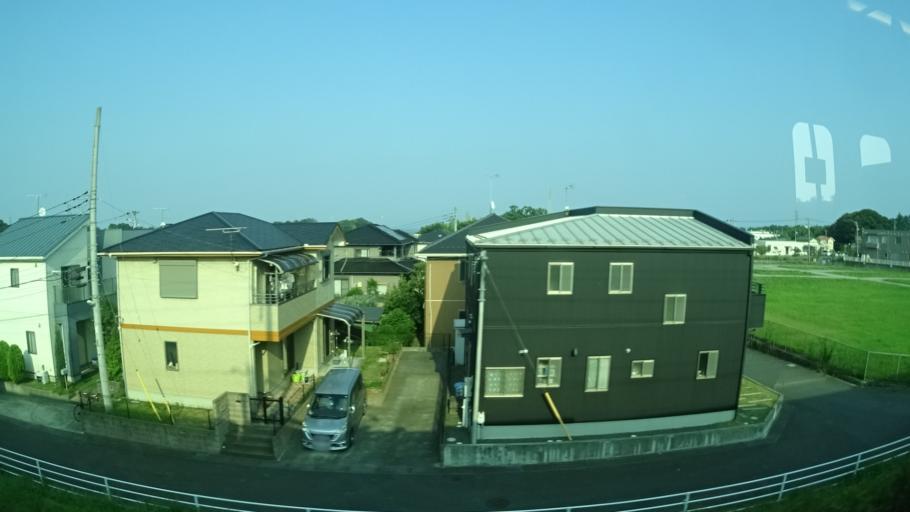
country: JP
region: Ibaraki
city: Hitachi
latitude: 36.6089
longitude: 140.6683
